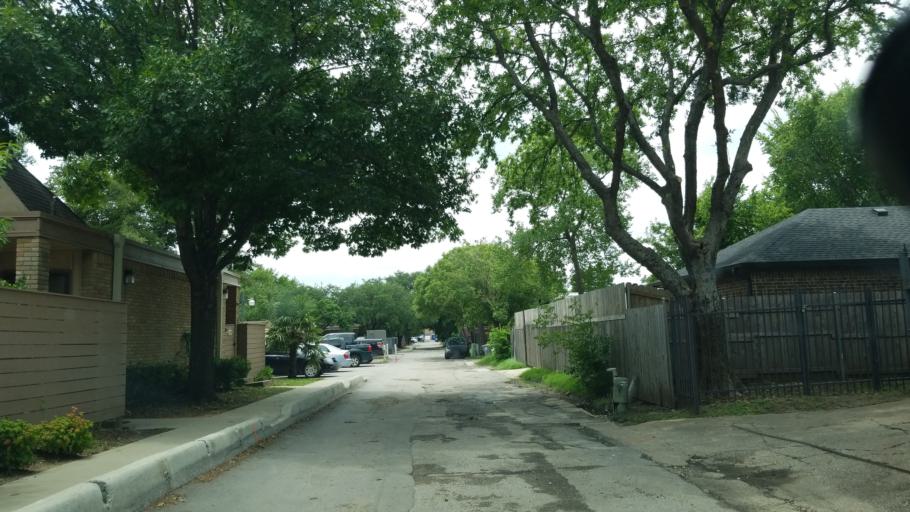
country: US
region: Texas
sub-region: Dallas County
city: Farmers Branch
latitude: 32.8769
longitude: -96.8742
